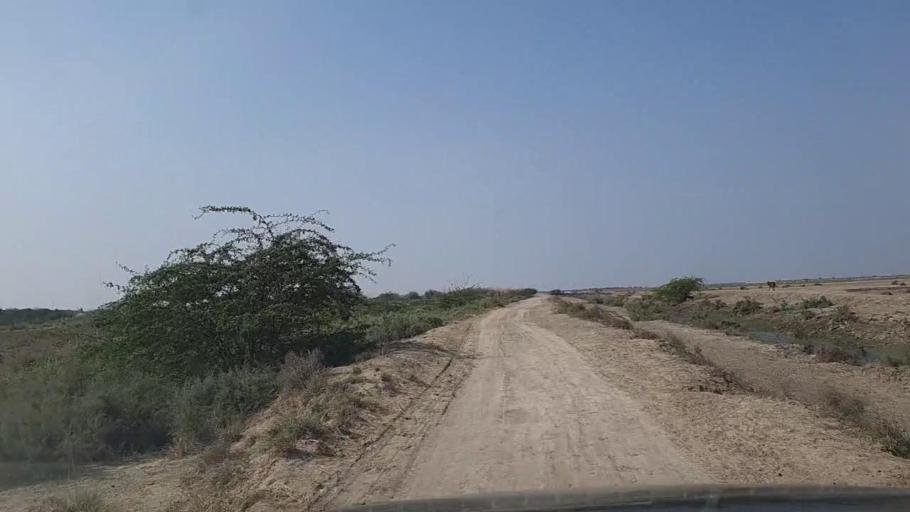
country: PK
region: Sindh
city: Gharo
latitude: 24.7046
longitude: 67.5767
